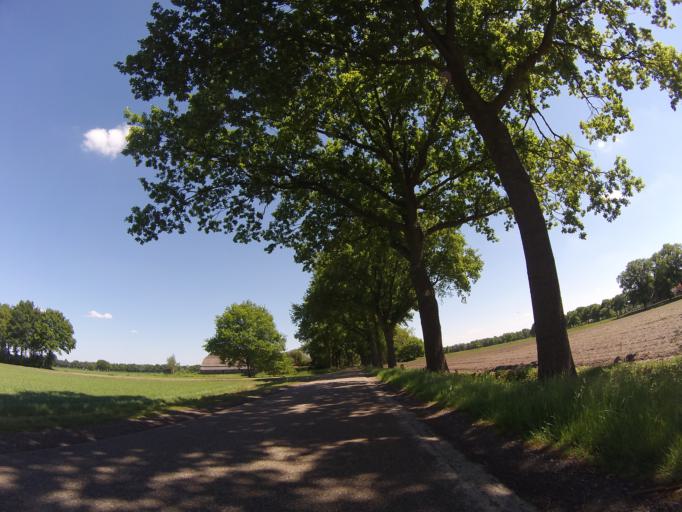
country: NL
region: Drenthe
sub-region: Gemeente Hoogeveen
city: Hoogeveen
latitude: 52.7901
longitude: 6.5691
